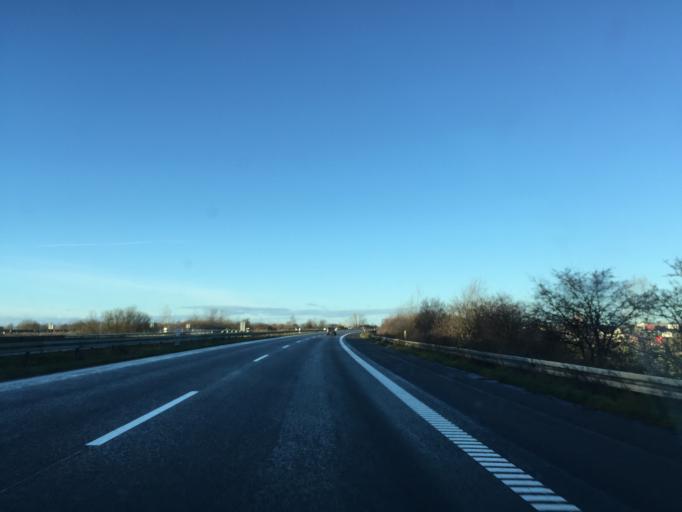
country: DK
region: South Denmark
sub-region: Middelfart Kommune
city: Norre Aby
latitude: 55.4656
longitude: 9.9036
